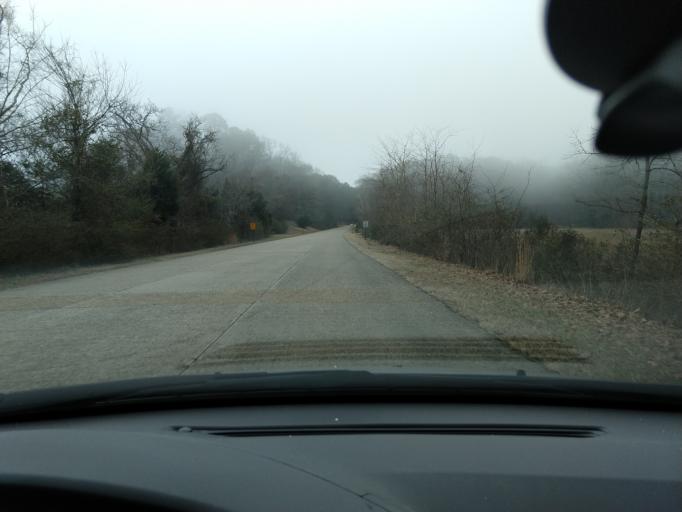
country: US
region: Virginia
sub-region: York County
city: Yorktown
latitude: 37.2428
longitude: -76.5261
